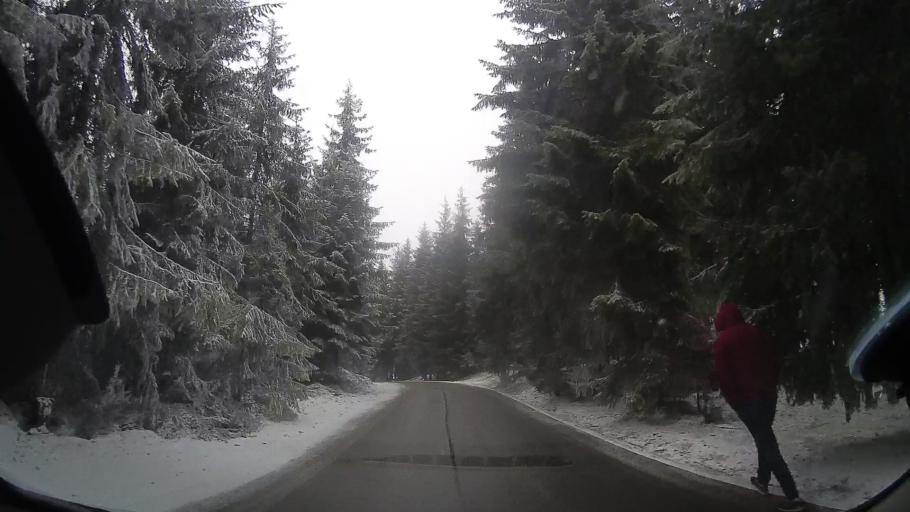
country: RO
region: Cluj
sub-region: Comuna Belis
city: Belis
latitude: 46.6389
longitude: 23.0509
